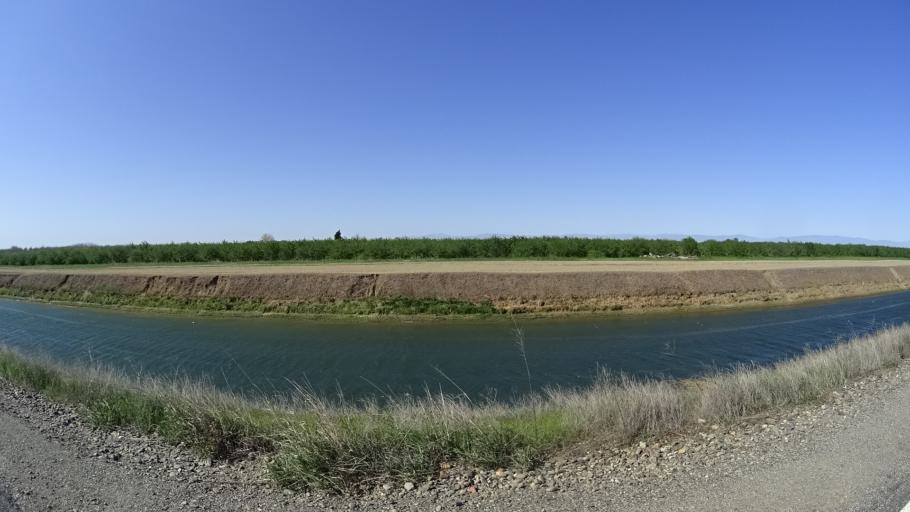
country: US
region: California
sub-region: Glenn County
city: Hamilton City
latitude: 39.7702
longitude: -122.0340
